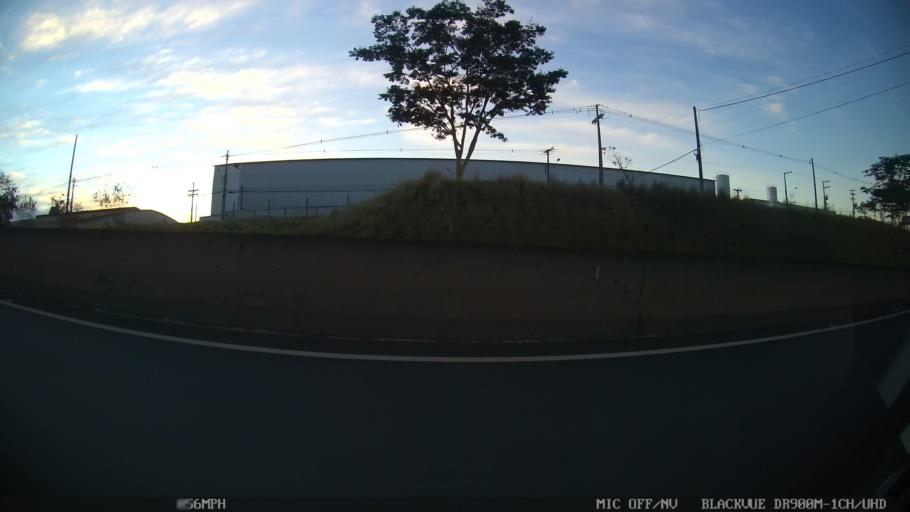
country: BR
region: Sao Paulo
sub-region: Catanduva
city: Catanduva
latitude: -21.1281
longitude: -49.0075
